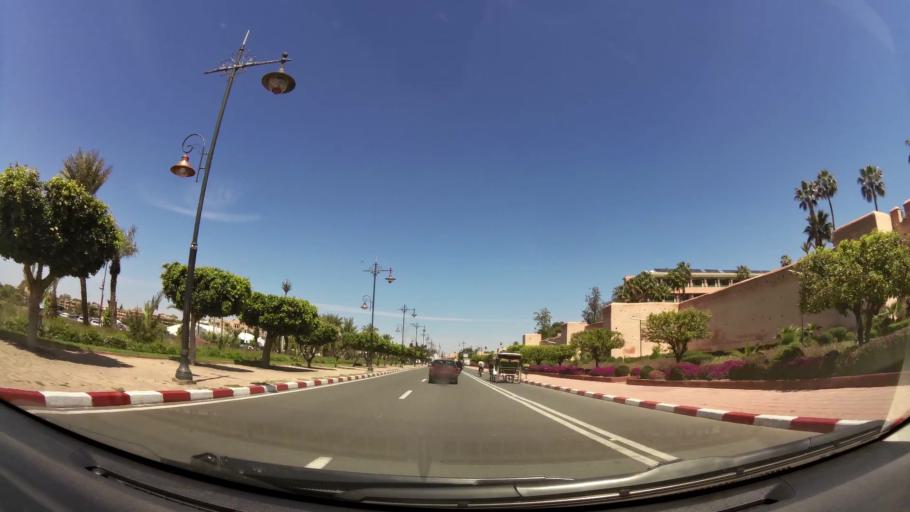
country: MA
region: Marrakech-Tensift-Al Haouz
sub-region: Marrakech
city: Marrakesh
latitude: 31.6200
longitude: -7.9982
